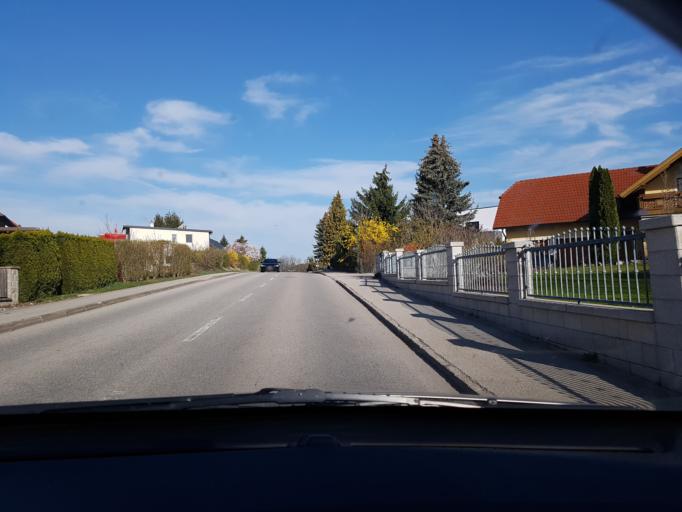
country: AT
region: Upper Austria
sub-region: Politischer Bezirk Linz-Land
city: Sankt Florian
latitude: 48.1433
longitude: 14.3767
